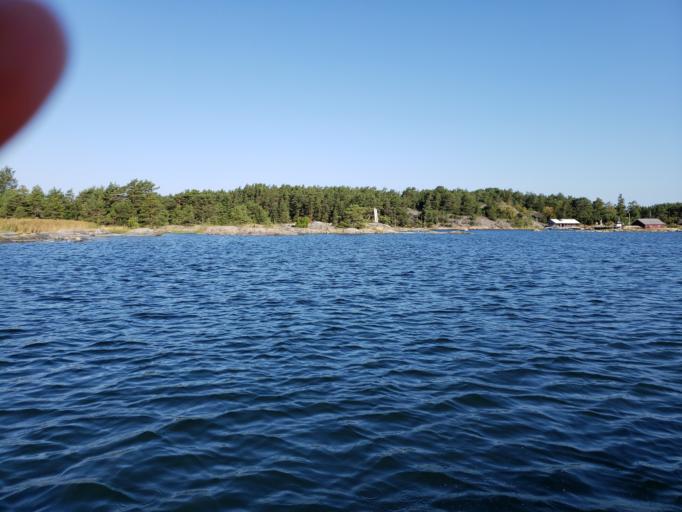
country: FI
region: Varsinais-Suomi
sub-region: Aboland-Turunmaa
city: Dragsfjaerd
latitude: 59.9054
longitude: 22.3672
